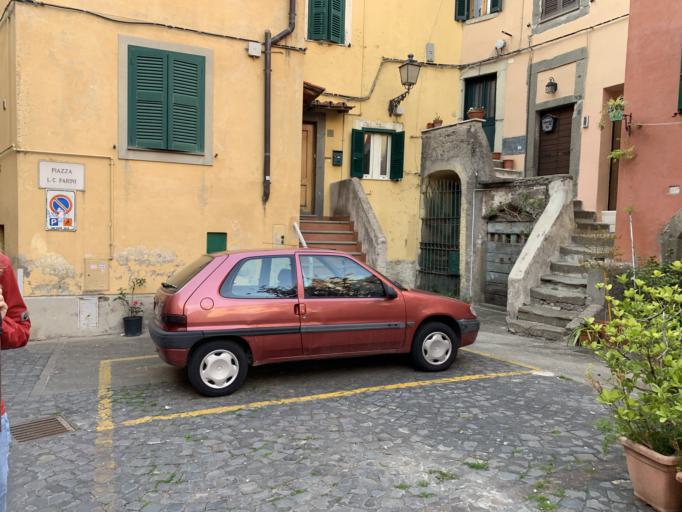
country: IT
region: Latium
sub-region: Citta metropolitana di Roma Capitale
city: Castel Gandolfo
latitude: 41.7690
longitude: 12.6606
